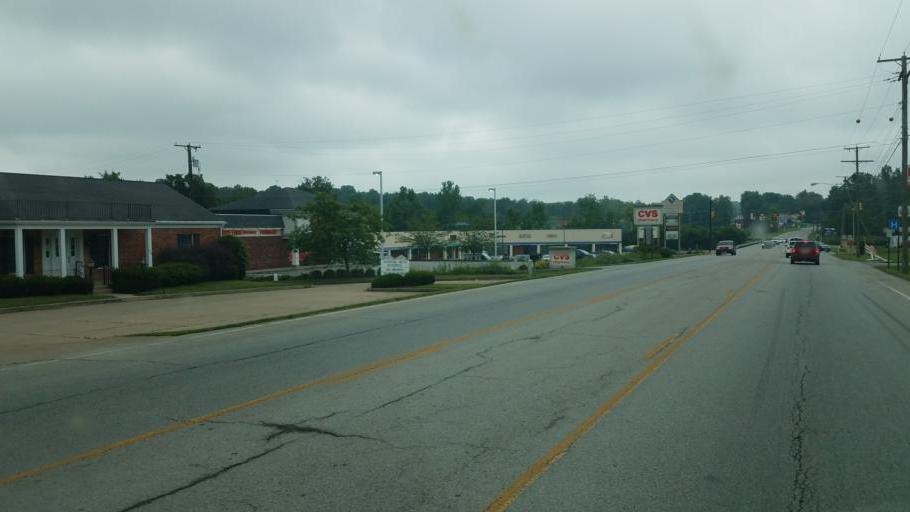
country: US
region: Ohio
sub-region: Highland County
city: Hillsboro
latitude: 39.2222
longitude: -83.6091
